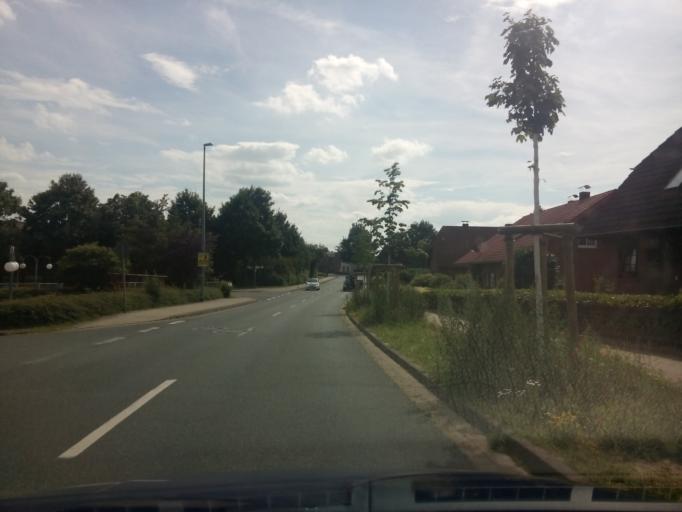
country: DE
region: Lower Saxony
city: Osterholz-Scharmbeck
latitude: 53.2294
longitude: 8.7987
